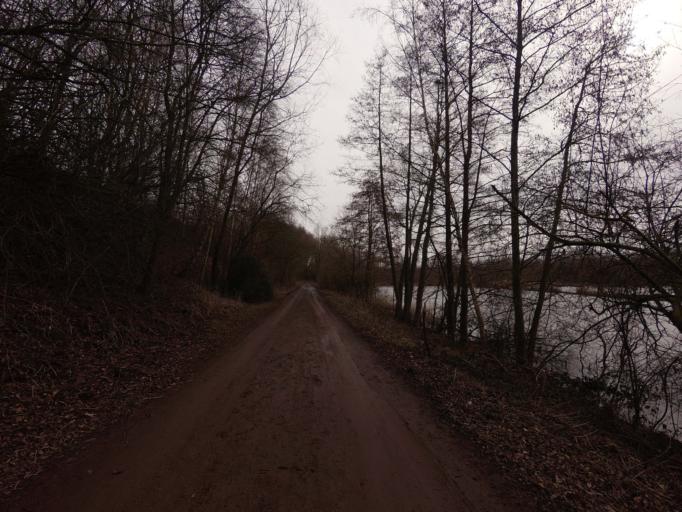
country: BE
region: Flanders
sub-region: Provincie Antwerpen
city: Niel
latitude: 51.1089
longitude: 4.3433
